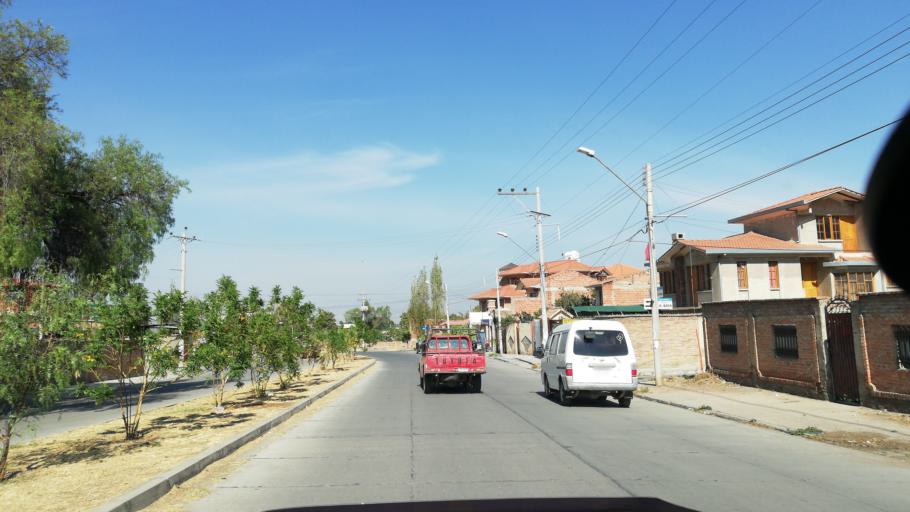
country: BO
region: Cochabamba
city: Cochabamba
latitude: -17.3604
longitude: -66.1875
